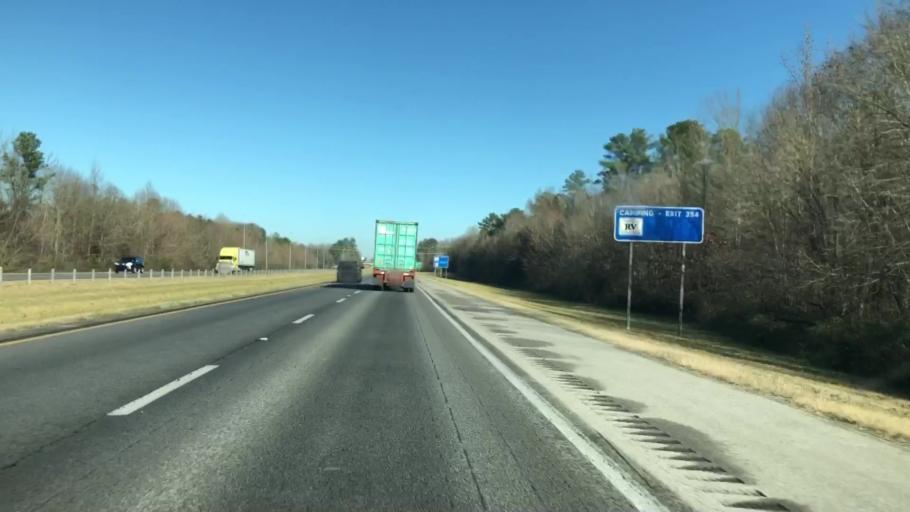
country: US
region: Alabama
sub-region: Limestone County
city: Athens
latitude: 34.8186
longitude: -86.9387
